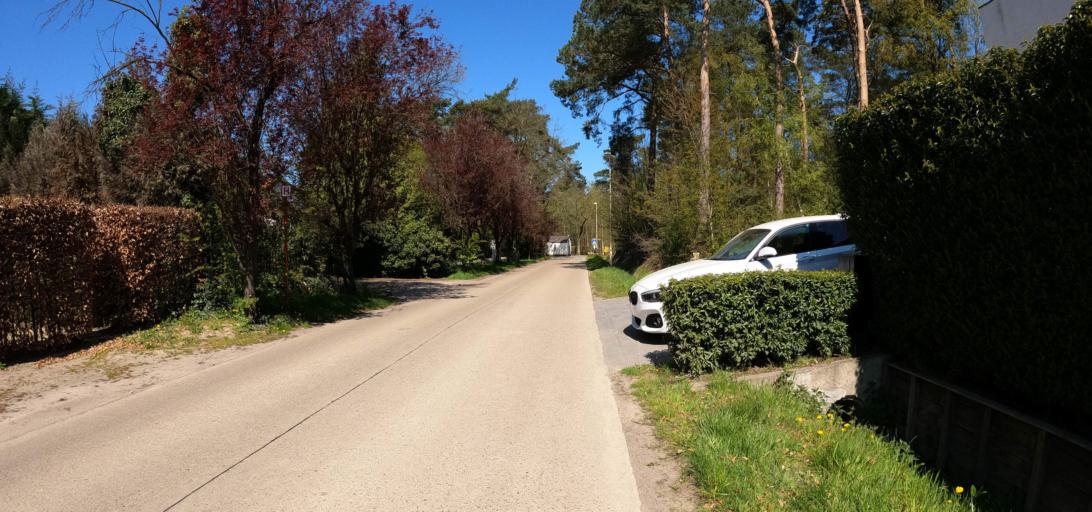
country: BE
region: Flanders
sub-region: Provincie Antwerpen
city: Zandhoven
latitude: 51.2377
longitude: 4.6299
